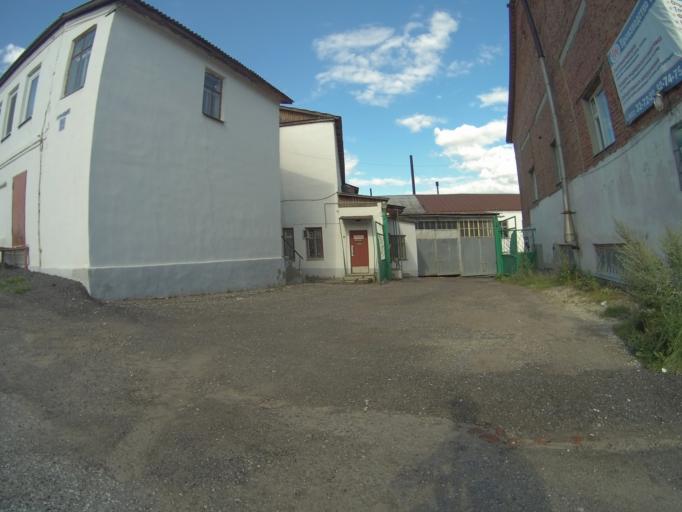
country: RU
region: Vladimir
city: Vladimir
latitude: 56.1198
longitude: 40.4001
